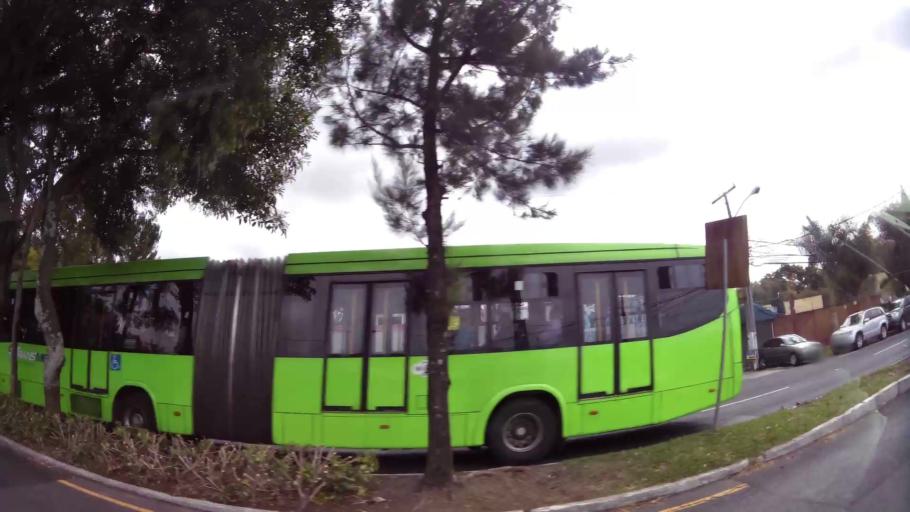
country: GT
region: Guatemala
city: Santa Catarina Pinula
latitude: 14.5842
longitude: -90.5230
